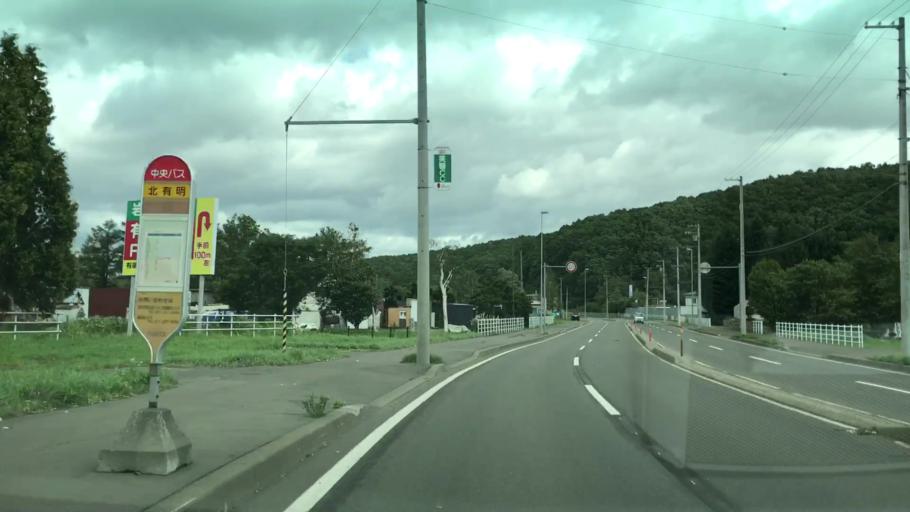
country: JP
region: Hokkaido
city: Kitahiroshima
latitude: 42.9651
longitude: 141.4546
